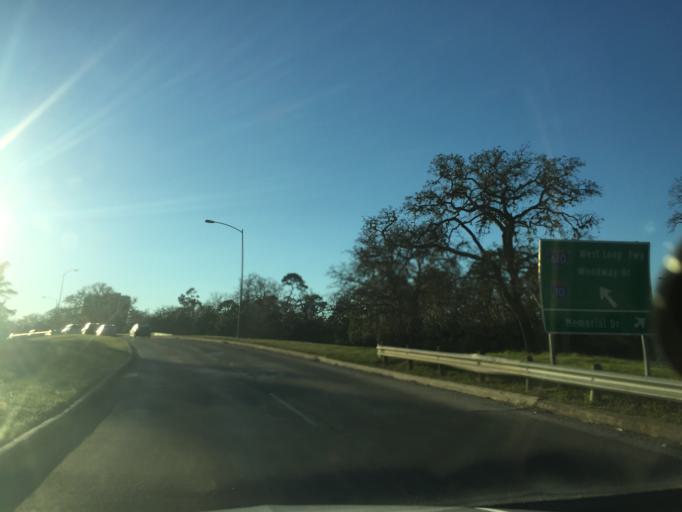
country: US
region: Texas
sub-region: Harris County
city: Hunters Creek Village
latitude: 29.7687
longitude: -95.4491
